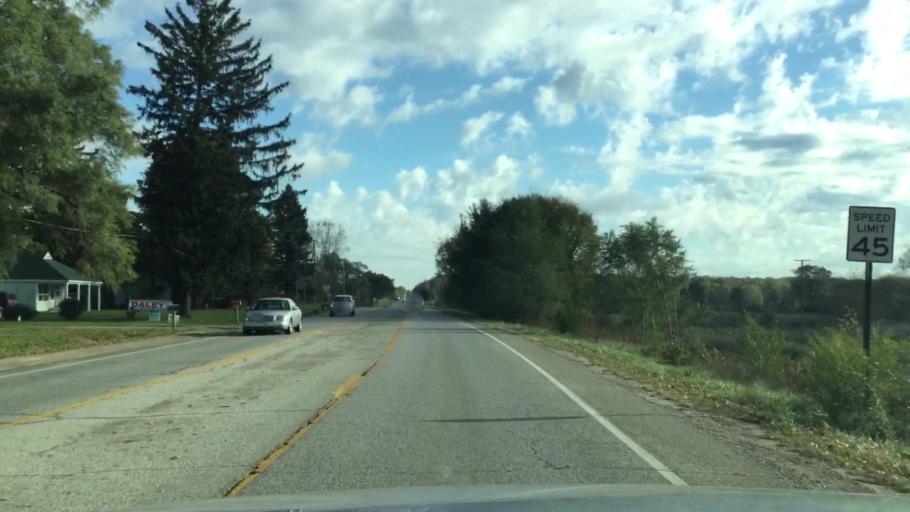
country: US
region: Michigan
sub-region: Lapeer County
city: Lapeer
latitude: 43.0434
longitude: -83.3612
